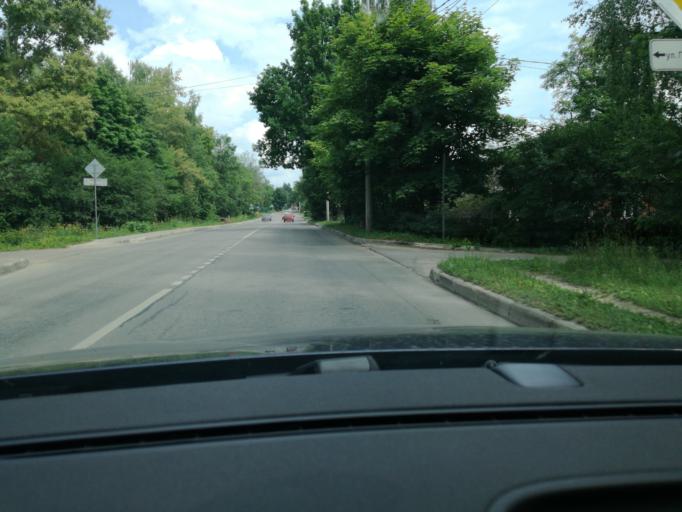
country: RU
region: Moskovskaya
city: Sergiyev Posad
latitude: 56.2926
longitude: 38.1089
